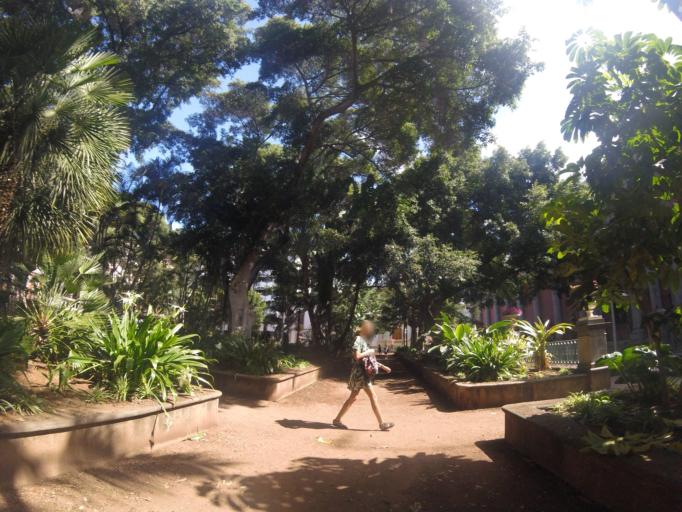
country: ES
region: Canary Islands
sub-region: Provincia de Santa Cruz de Tenerife
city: Santa Cruz de Tenerife
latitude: 28.4681
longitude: -16.2501
